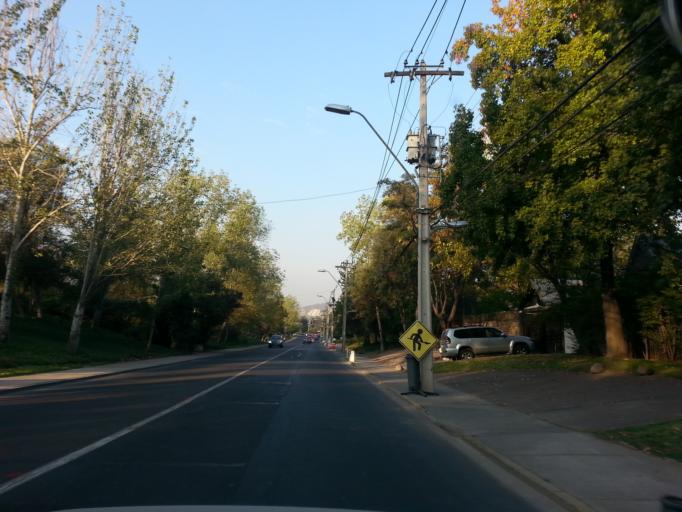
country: CL
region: Santiago Metropolitan
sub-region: Provincia de Santiago
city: Villa Presidente Frei, Nunoa, Santiago, Chile
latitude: -33.3800
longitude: -70.5730
